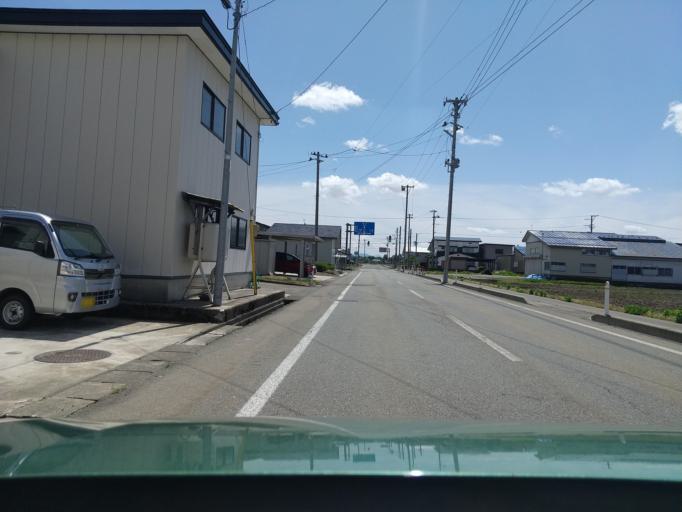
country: JP
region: Akita
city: Yokotemachi
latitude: 39.3656
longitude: 140.5365
